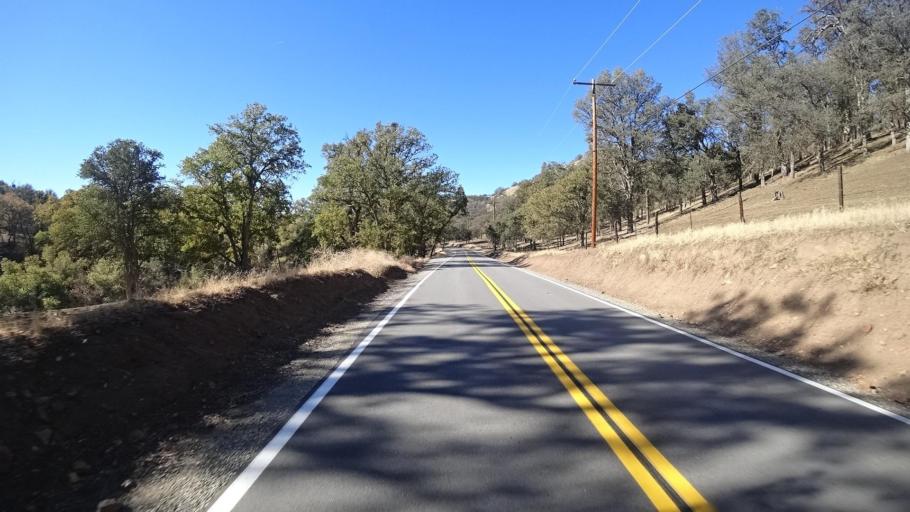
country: US
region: California
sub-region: Kern County
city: Alta Sierra
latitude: 35.7321
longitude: -118.6726
